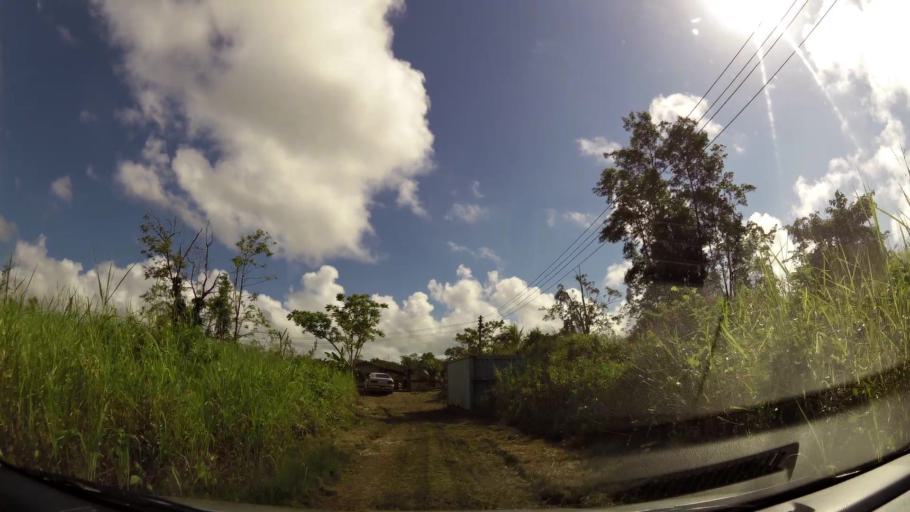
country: SR
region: Commewijne
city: Nieuw Amsterdam
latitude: 5.8780
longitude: -55.1101
